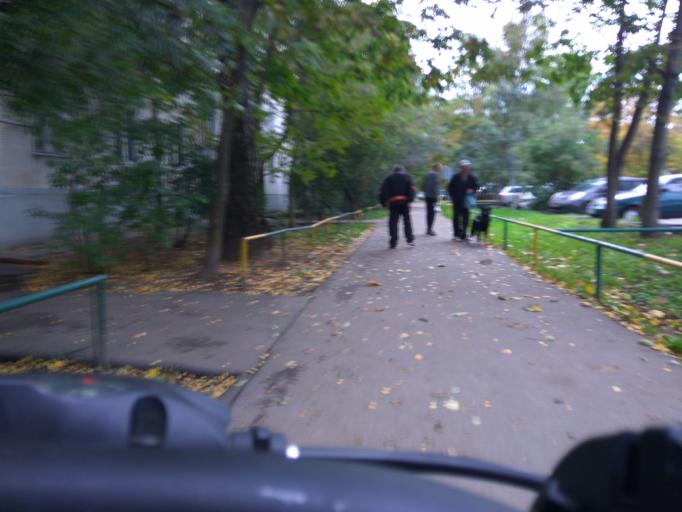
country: RU
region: Moscow
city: Kozeyevo
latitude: 55.8794
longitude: 37.6226
